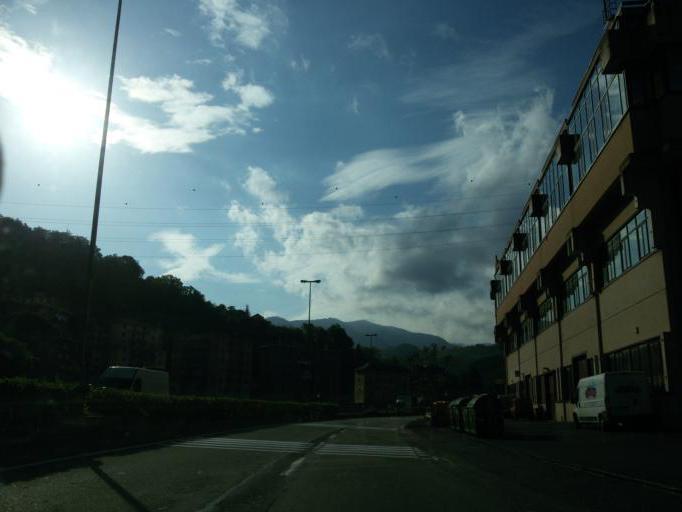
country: IT
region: Liguria
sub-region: Provincia di Genova
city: Piccarello
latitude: 44.4527
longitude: 8.9902
